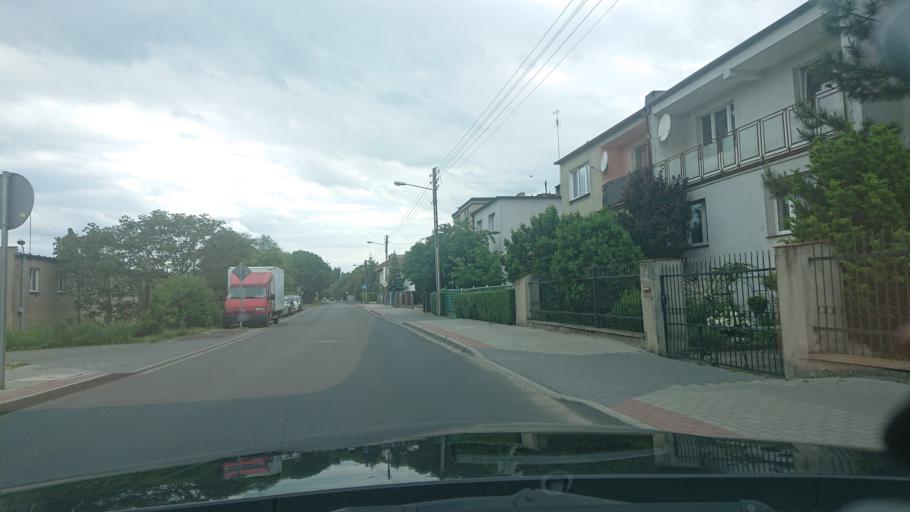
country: PL
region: Greater Poland Voivodeship
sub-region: Powiat gnieznienski
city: Gniezno
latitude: 52.5322
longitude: 17.6176
